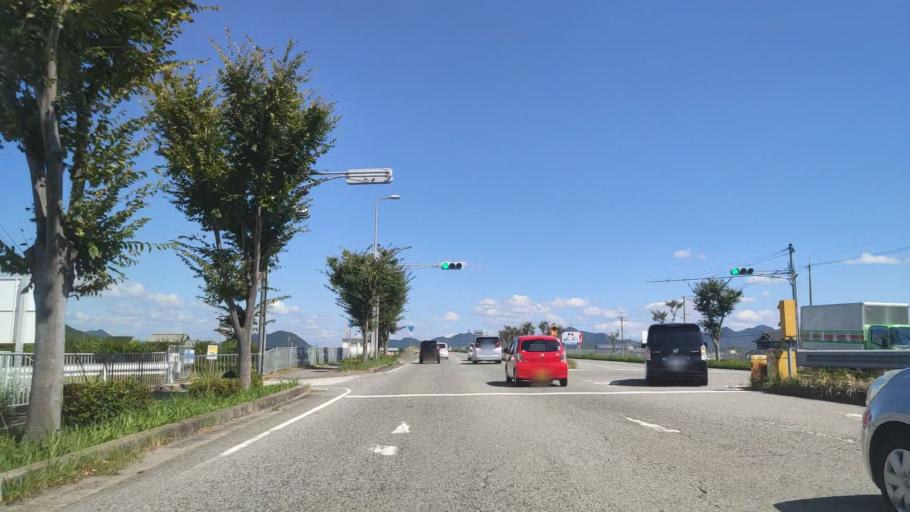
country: JP
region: Hyogo
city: Yashiro
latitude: 34.9173
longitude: 134.9573
